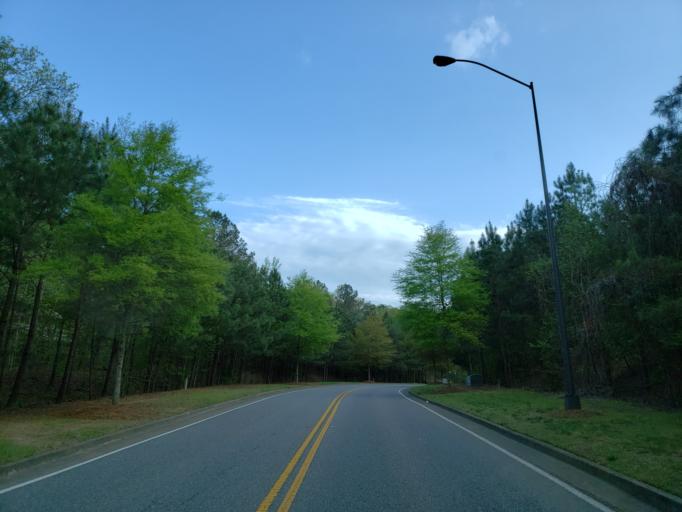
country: US
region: Georgia
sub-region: Cherokee County
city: Canton
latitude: 34.2901
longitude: -84.4632
